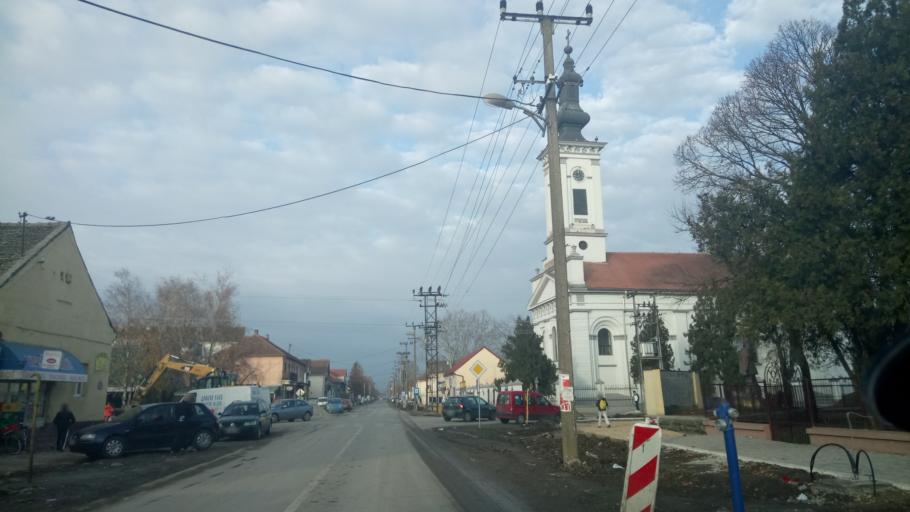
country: RS
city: Vojka
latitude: 44.9352
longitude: 20.1515
